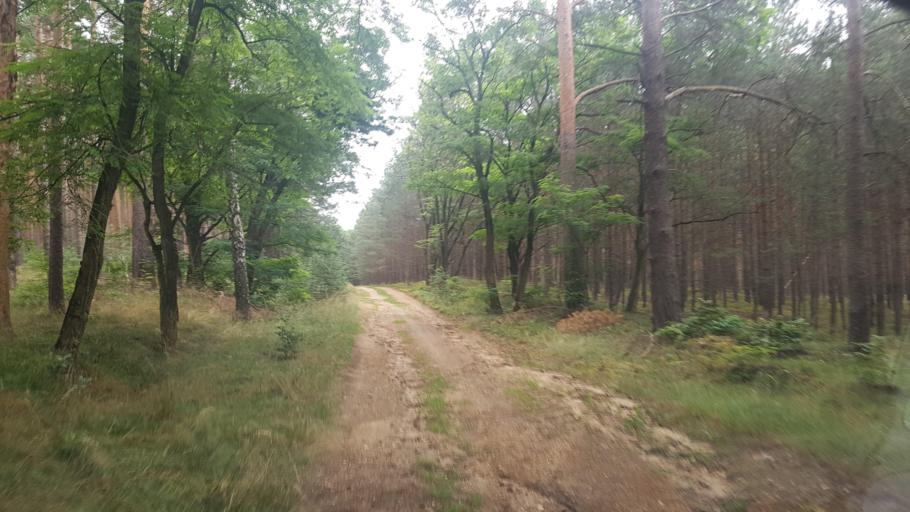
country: DE
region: Brandenburg
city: Crinitz
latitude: 51.7438
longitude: 13.7906
